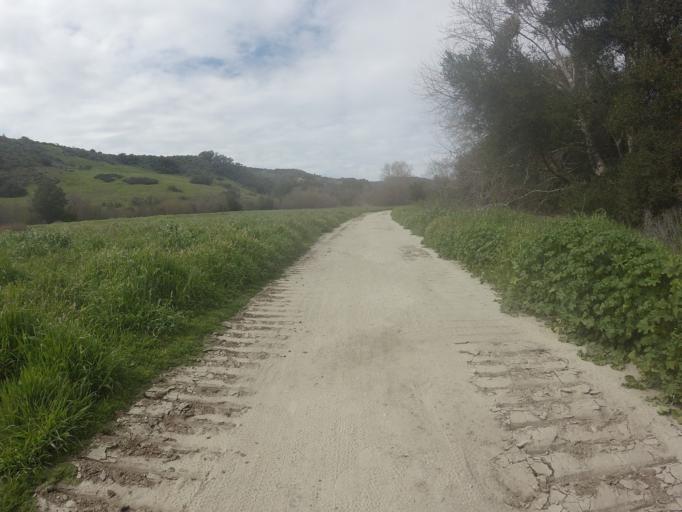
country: US
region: California
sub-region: Orange County
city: Aliso Viejo
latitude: 33.5583
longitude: -117.7409
